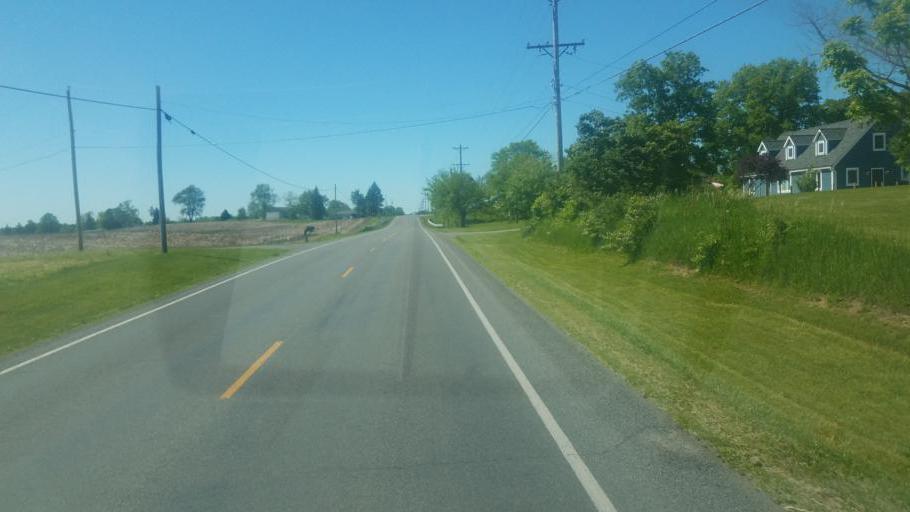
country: US
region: Ohio
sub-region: Logan County
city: Bellefontaine
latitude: 40.3909
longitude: -83.7910
